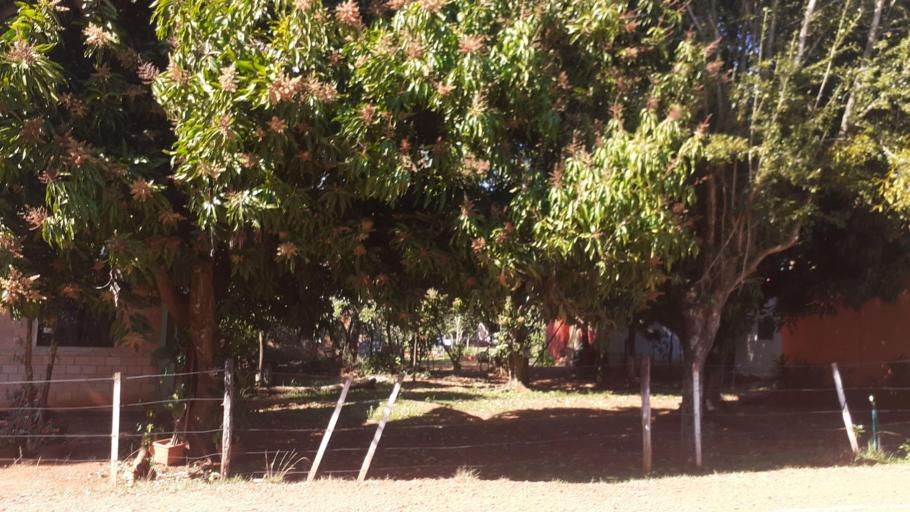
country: PY
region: Misiones
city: San Juan Bautista
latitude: -26.6639
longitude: -57.1243
